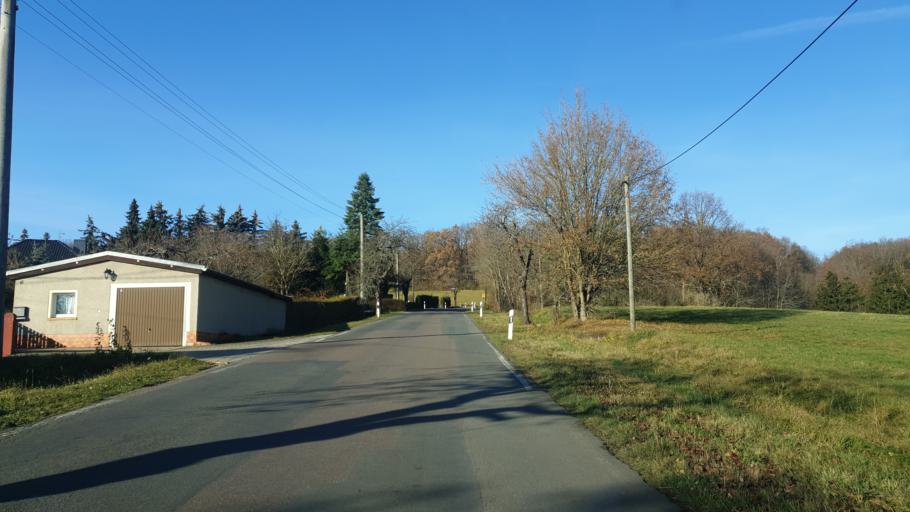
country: DE
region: Saxony-Anhalt
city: Wetterzeube
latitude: 51.0086
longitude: 12.0065
